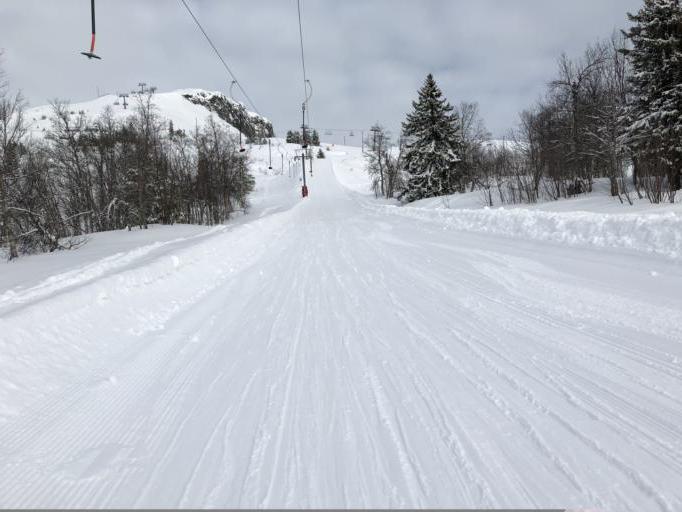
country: NO
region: Oppland
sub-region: Gausdal
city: Segalstad bru
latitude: 61.3419
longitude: 10.0875
